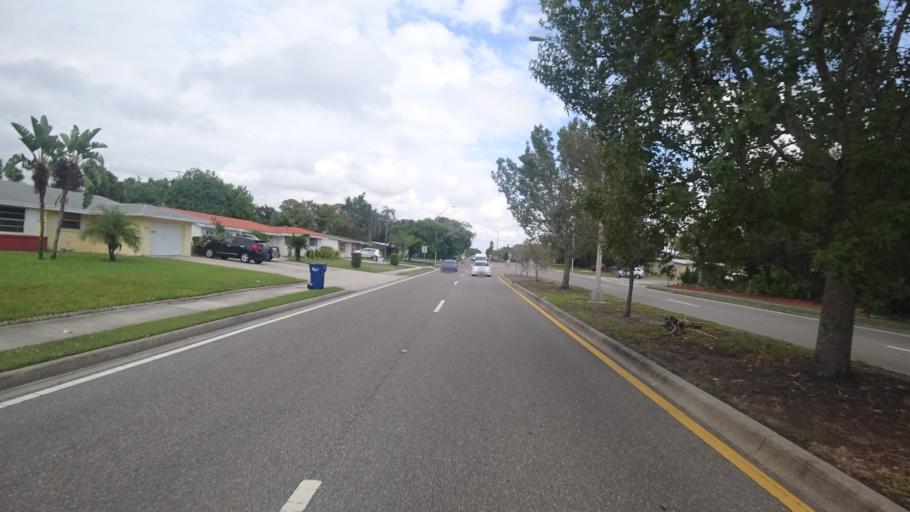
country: US
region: Florida
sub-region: Manatee County
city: Bayshore Gardens
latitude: 27.4313
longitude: -82.5828
